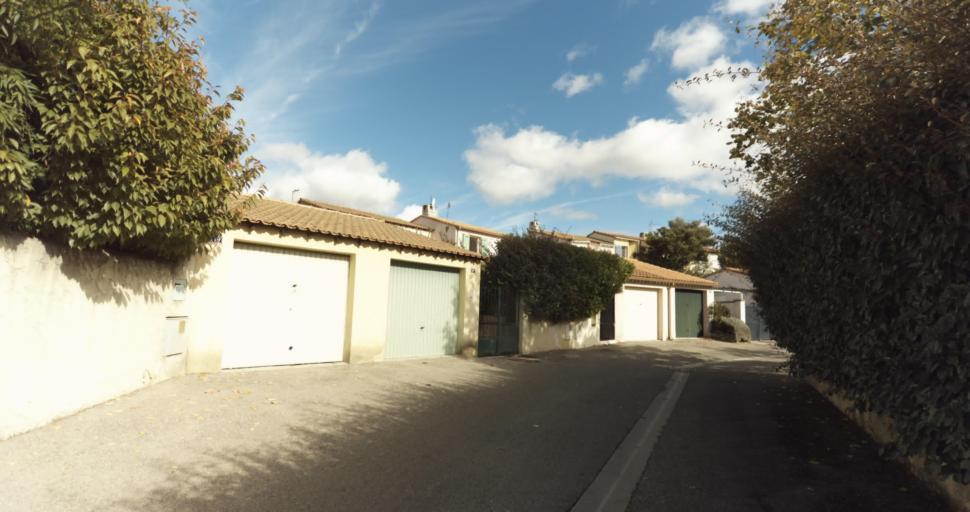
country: FR
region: Provence-Alpes-Cote d'Azur
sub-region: Departement des Bouches-du-Rhone
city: Venelles
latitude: 43.5997
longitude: 5.4892
